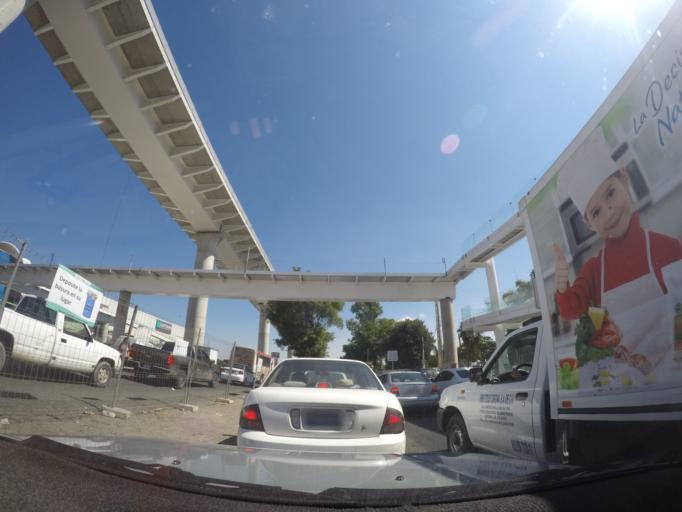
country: MX
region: Jalisco
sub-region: Zapotlanejo
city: La Mezquitera
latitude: 20.5389
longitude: -103.0207
